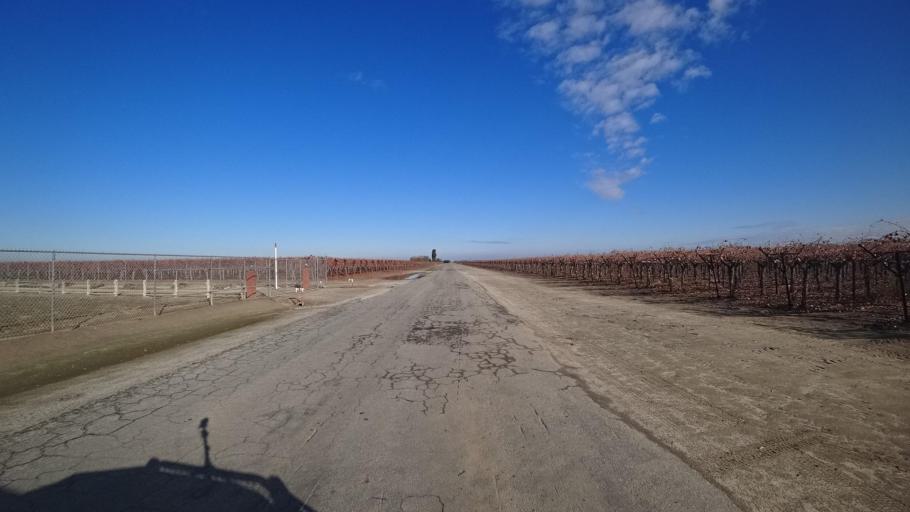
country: US
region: California
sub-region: Kern County
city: Delano
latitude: 35.7257
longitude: -119.3030
